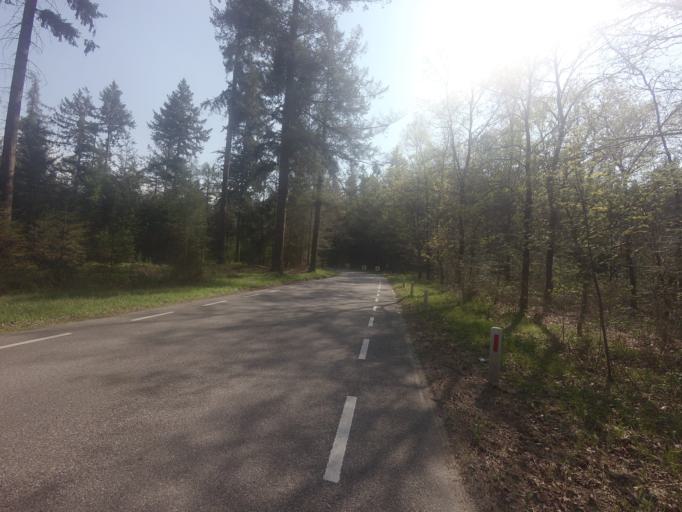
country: NL
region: North Holland
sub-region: Gemeente Hilversum
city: Hilversum
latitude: 52.1856
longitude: 5.2255
